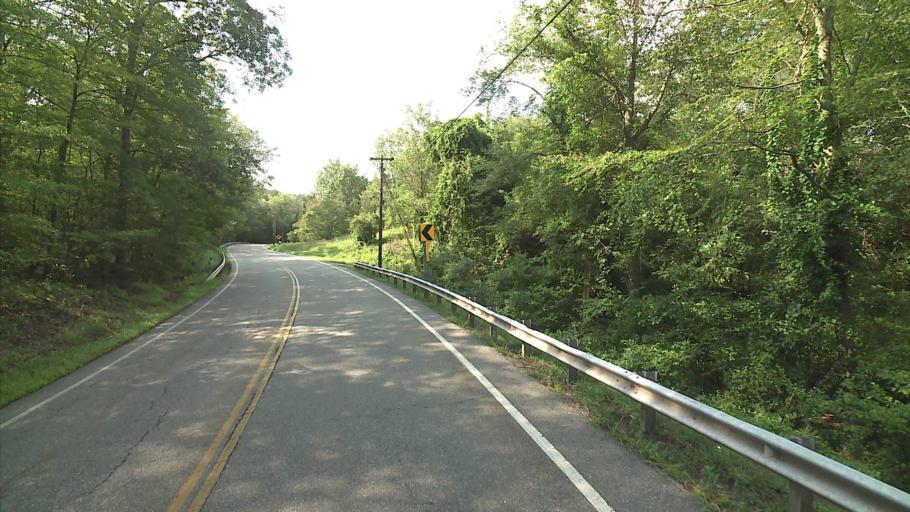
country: US
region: Connecticut
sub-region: Middlesex County
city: East Haddam
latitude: 41.4809
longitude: -72.4689
